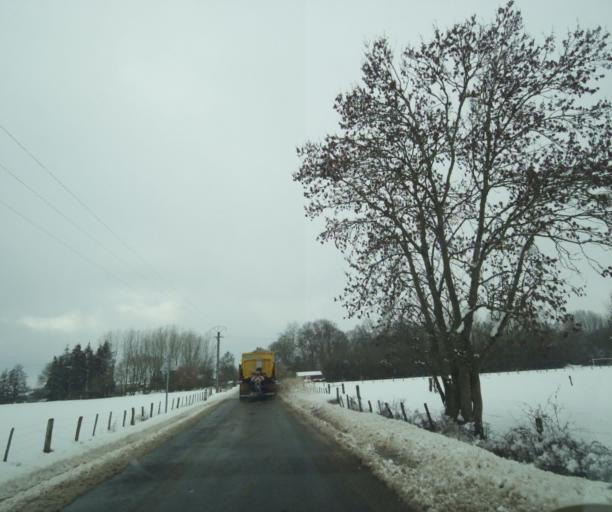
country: FR
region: Champagne-Ardenne
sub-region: Departement de la Haute-Marne
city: Montier-en-Der
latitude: 48.4948
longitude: 4.7051
